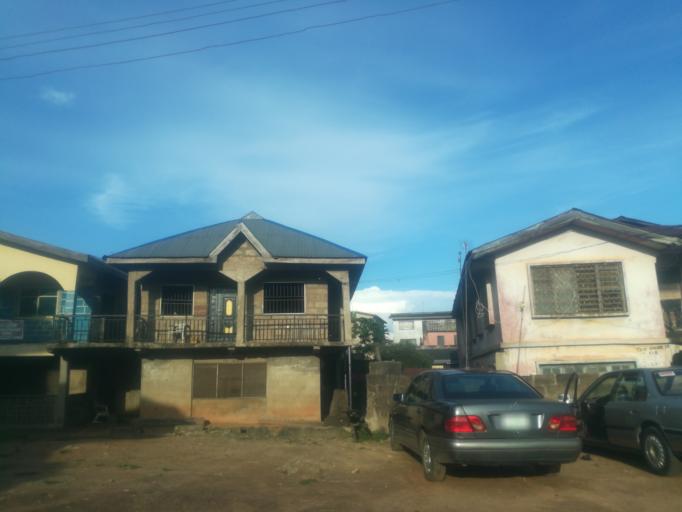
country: NG
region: Oyo
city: Ibadan
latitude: 7.3496
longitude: 3.8878
